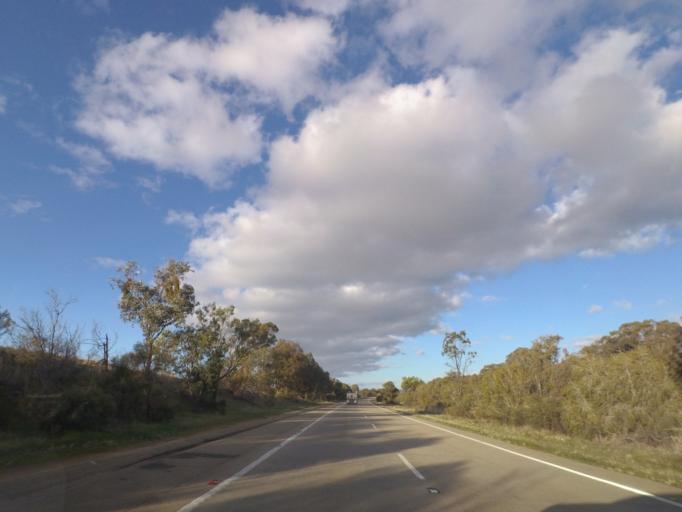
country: AU
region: New South Wales
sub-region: Yass Valley
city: Yass
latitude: -34.8011
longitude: 148.4993
